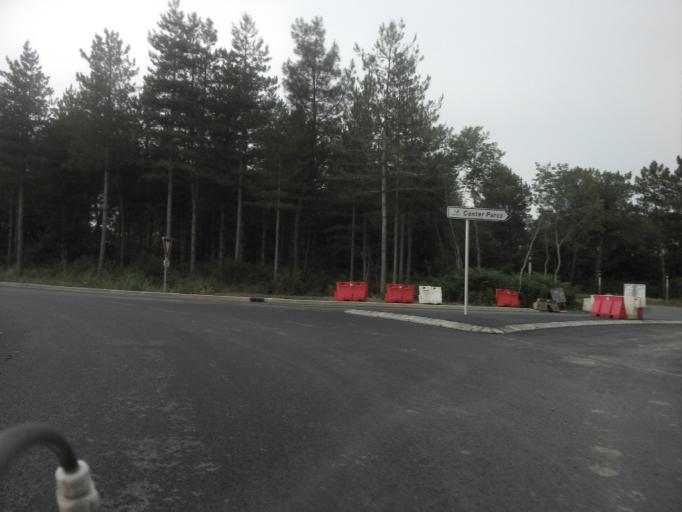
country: FR
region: Pays de la Loire
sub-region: Departement de Maine-et-Loire
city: Breze
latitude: 47.0932
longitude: -0.0006
